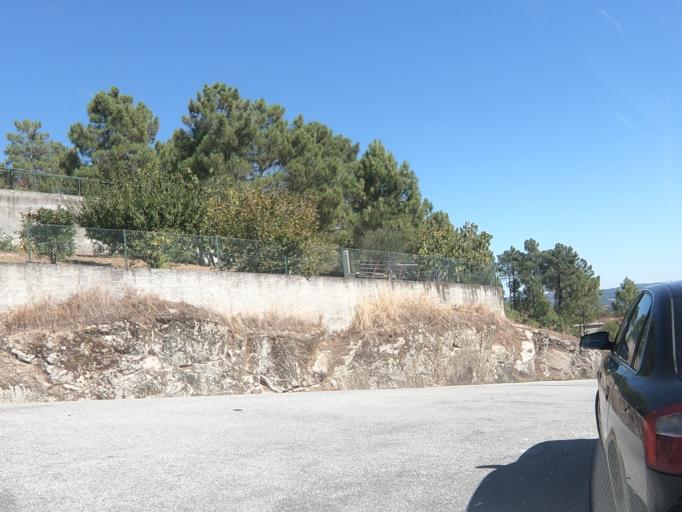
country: PT
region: Vila Real
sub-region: Santa Marta de Penaguiao
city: Santa Marta de Penaguiao
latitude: 41.2597
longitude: -7.7831
